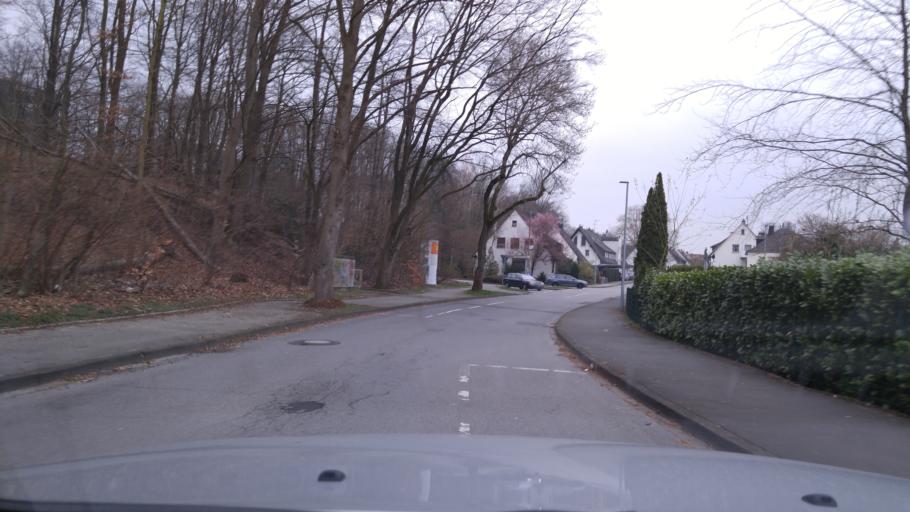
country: DE
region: North Rhine-Westphalia
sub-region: Regierungsbezirk Arnsberg
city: Menden
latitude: 51.4345
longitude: 7.7710
